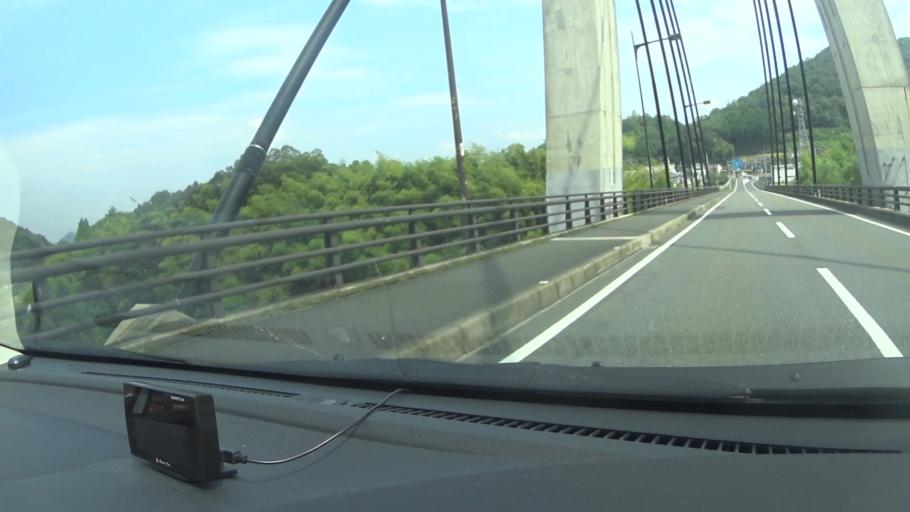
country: JP
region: Kyoto
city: Ayabe
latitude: 35.2908
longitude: 135.2665
